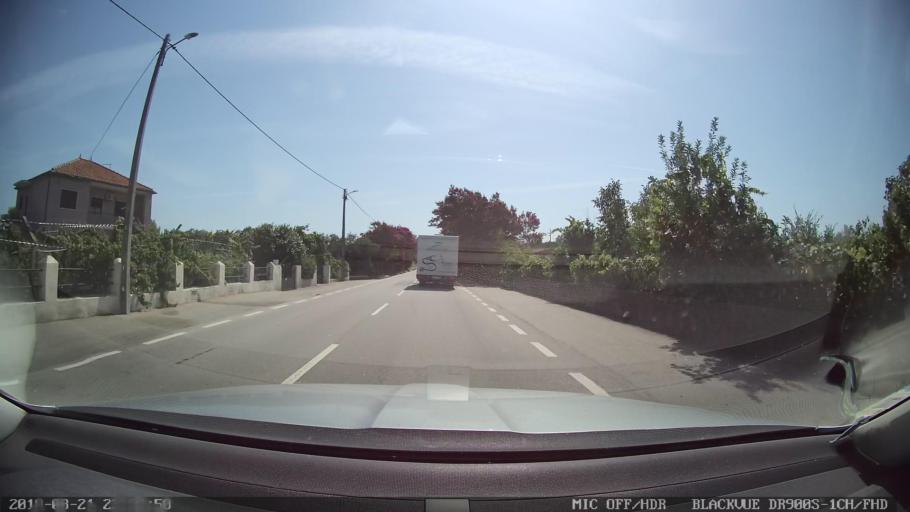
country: PT
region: Guarda
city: Alcains
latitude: 39.8794
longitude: -7.3949
